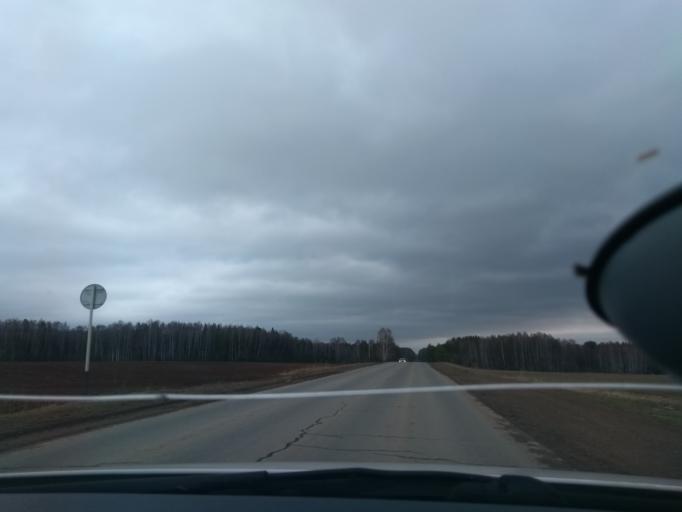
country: RU
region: Perm
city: Kungur
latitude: 57.3465
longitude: 56.7922
